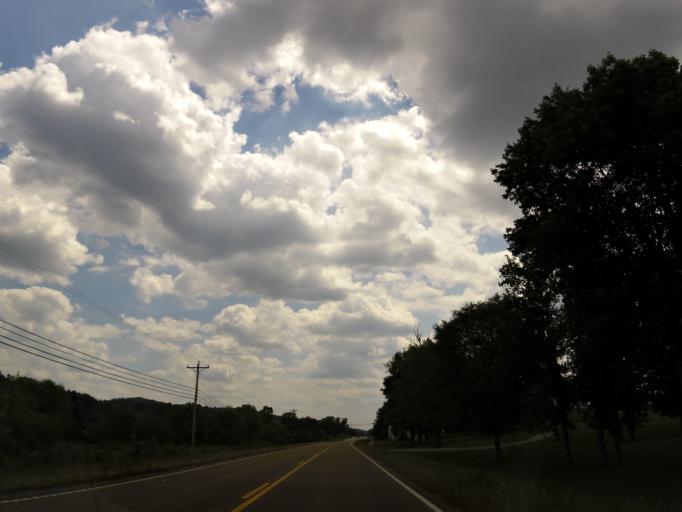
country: US
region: Tennessee
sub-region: Bledsoe County
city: Pikeville
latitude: 35.5136
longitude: -85.2816
